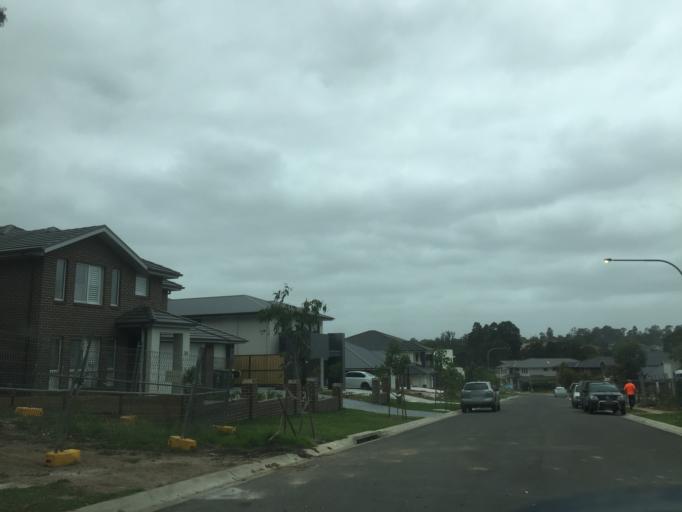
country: AU
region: New South Wales
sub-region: The Hills Shire
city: Beaumont Hills
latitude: -33.7233
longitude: 150.9533
